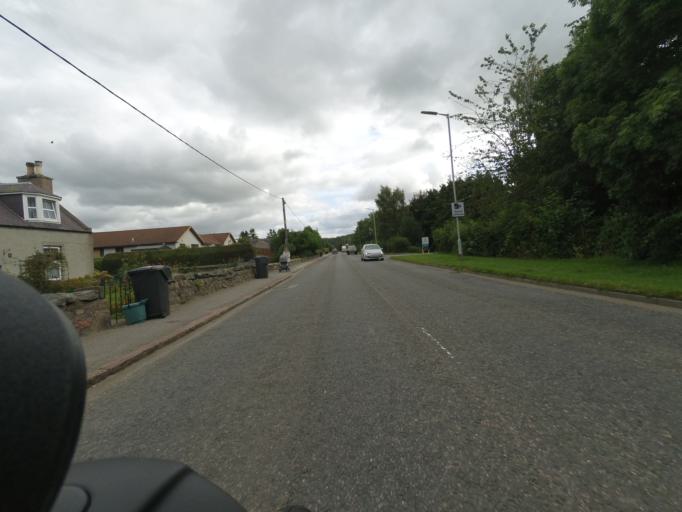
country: GB
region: Scotland
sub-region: Aberdeenshire
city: Banchory
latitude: 57.0577
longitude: -2.4708
